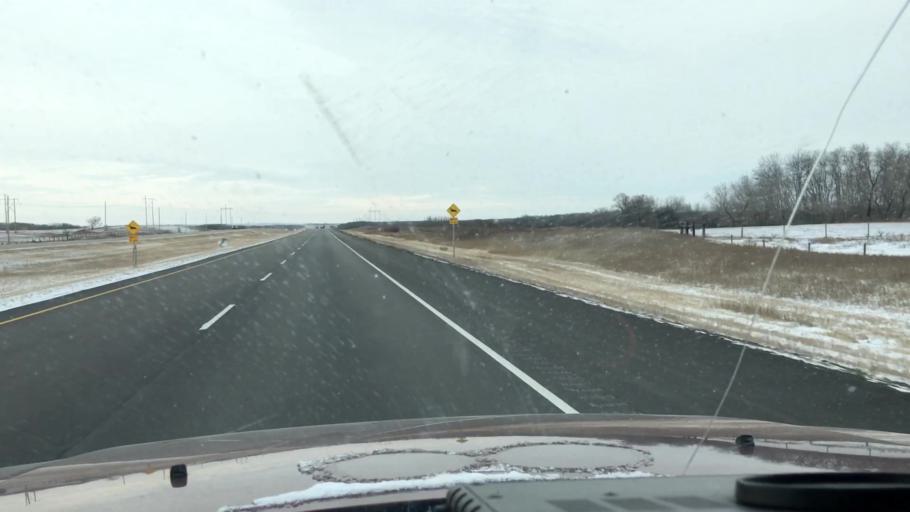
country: CA
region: Saskatchewan
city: Saskatoon
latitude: 51.8976
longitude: -106.5202
